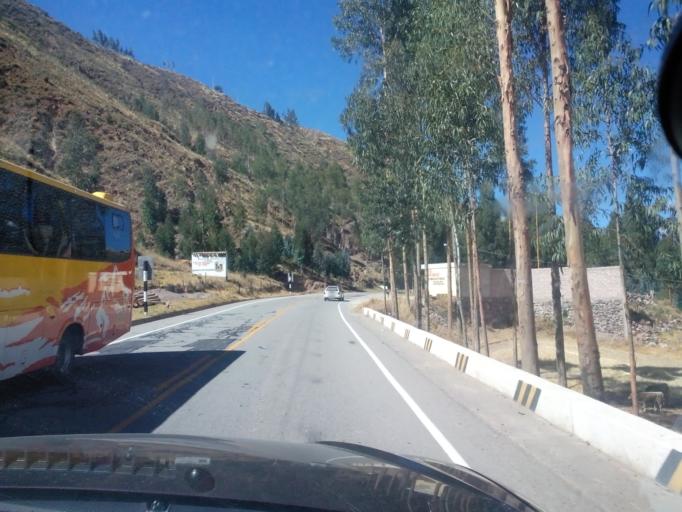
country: PE
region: Cusco
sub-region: Provincia de Canchis
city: Checacupe
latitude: -14.0326
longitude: -71.4514
